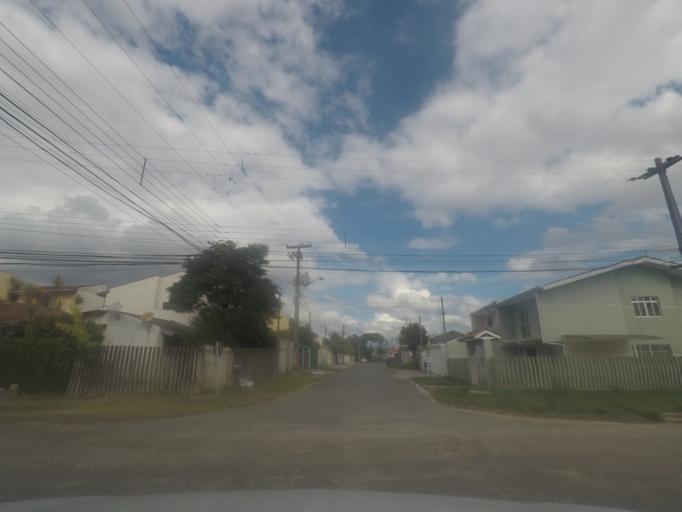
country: BR
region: Parana
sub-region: Pinhais
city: Pinhais
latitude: -25.4718
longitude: -49.2185
